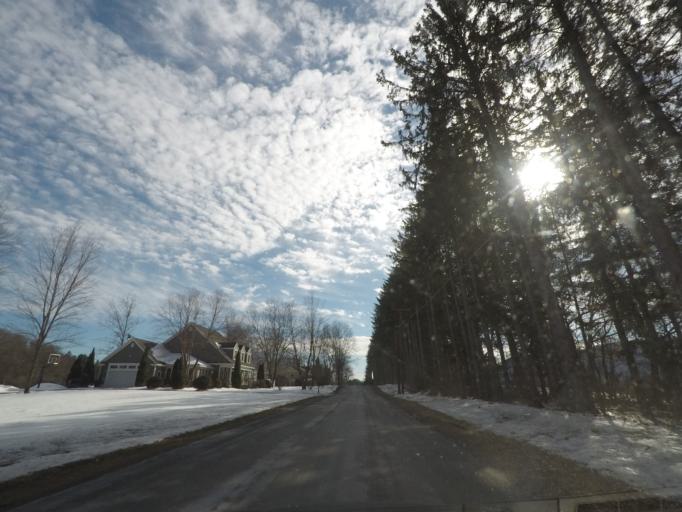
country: US
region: New York
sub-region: Albany County
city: Voorheesville
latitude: 42.6568
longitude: -73.9658
